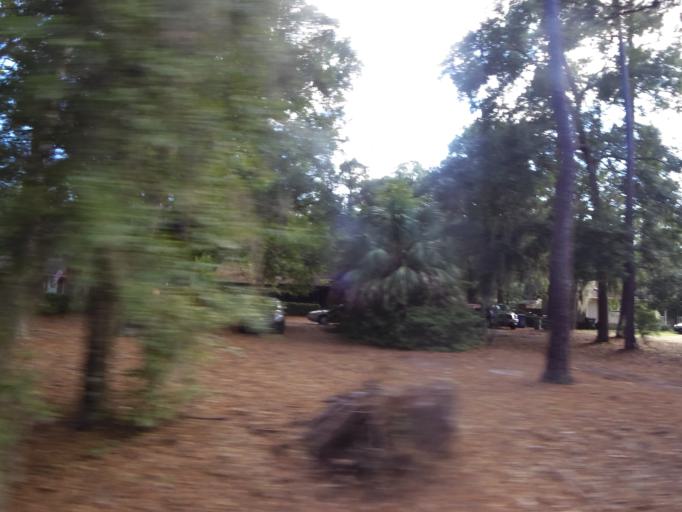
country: US
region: Georgia
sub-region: Glynn County
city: Country Club Estates
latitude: 31.2570
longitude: -81.4382
